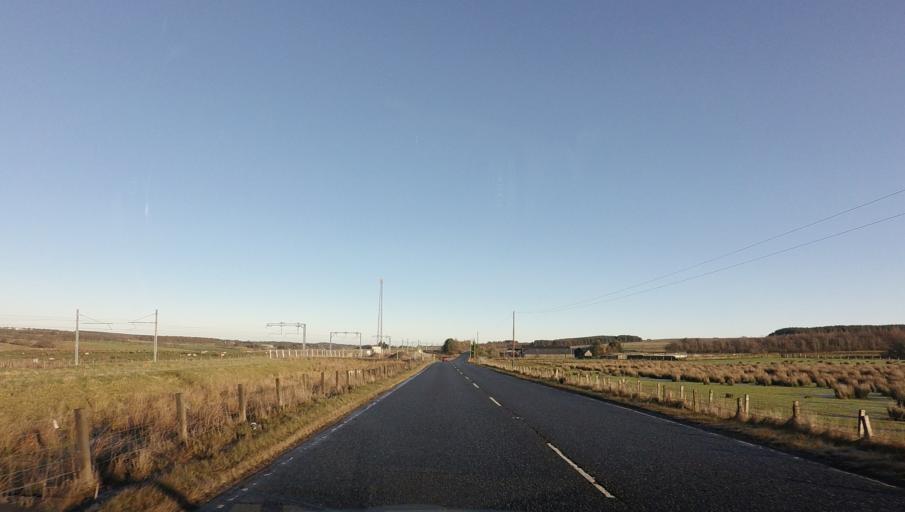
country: GB
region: Scotland
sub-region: West Lothian
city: Fauldhouse
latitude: 55.8207
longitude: -3.6883
